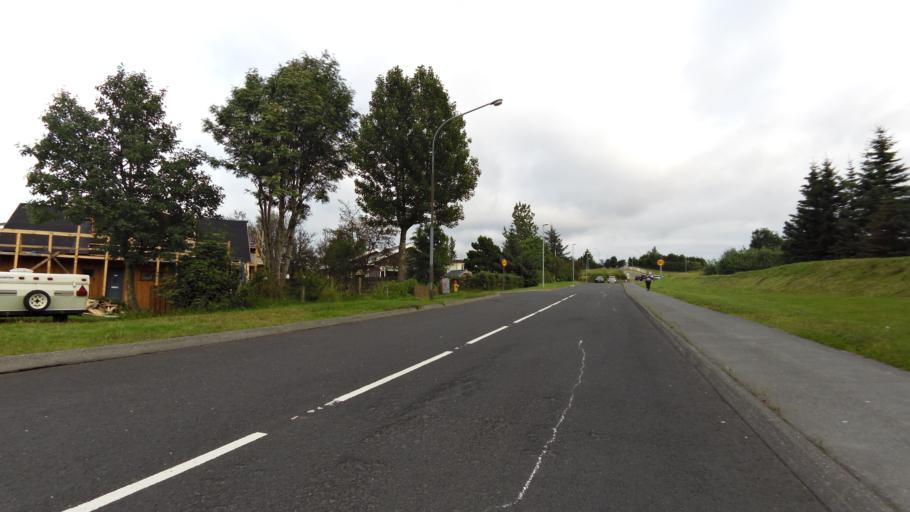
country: IS
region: Capital Region
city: Reykjavik
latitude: 64.1157
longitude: -21.8474
